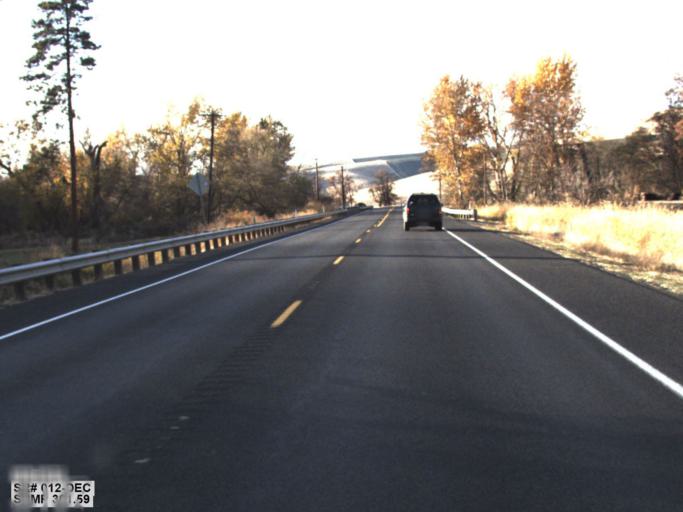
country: US
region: Washington
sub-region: Walla Walla County
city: Waitsburg
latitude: 46.2887
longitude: -118.0792
